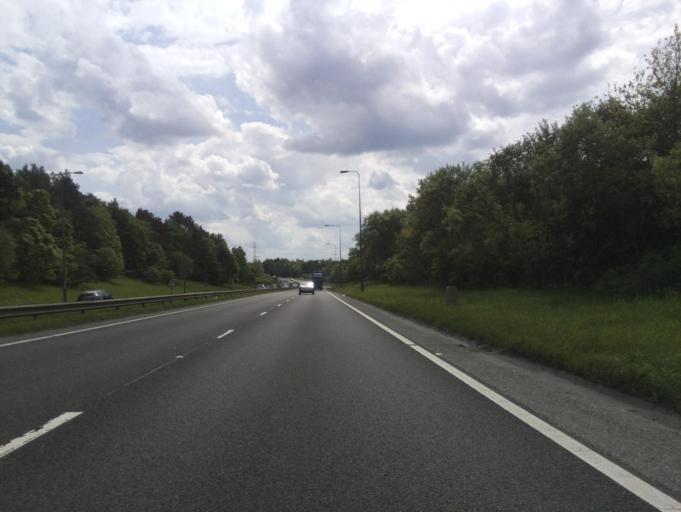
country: GB
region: England
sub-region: County Durham
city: Wingate
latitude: 54.7458
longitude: -1.3644
